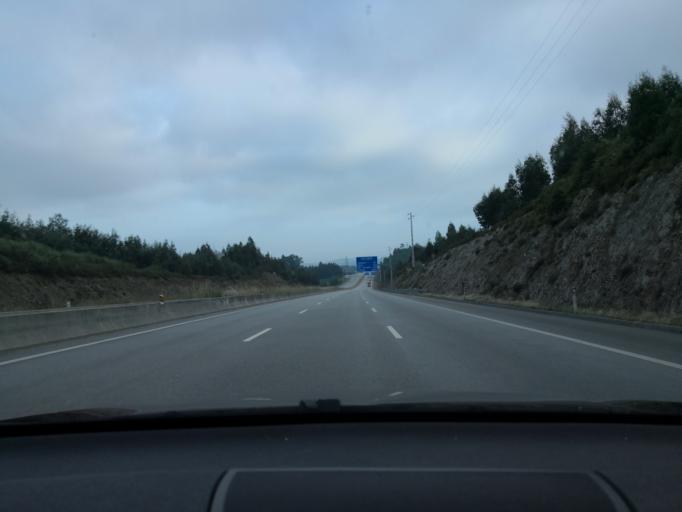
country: PT
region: Porto
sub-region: Gondomar
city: Foz do Sousa
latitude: 41.0868
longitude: -8.4548
